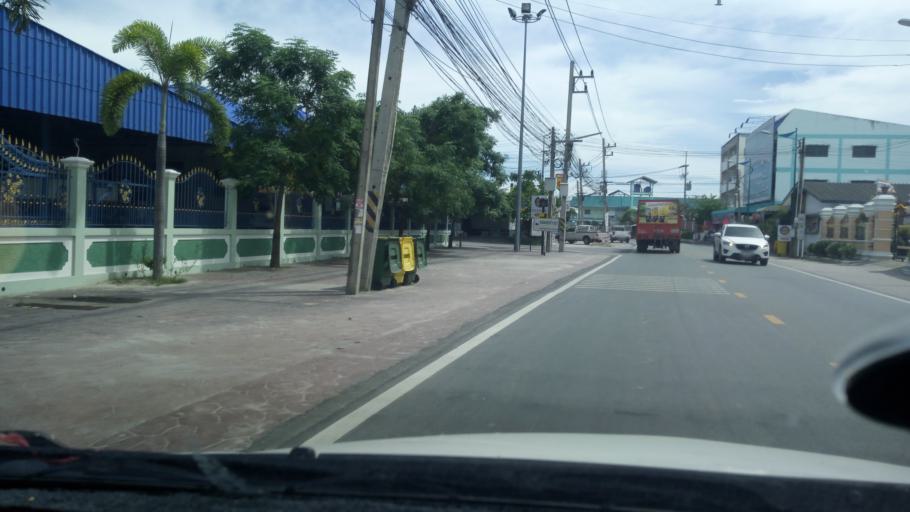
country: TH
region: Chon Buri
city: Chon Buri
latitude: 13.4197
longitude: 101.0325
